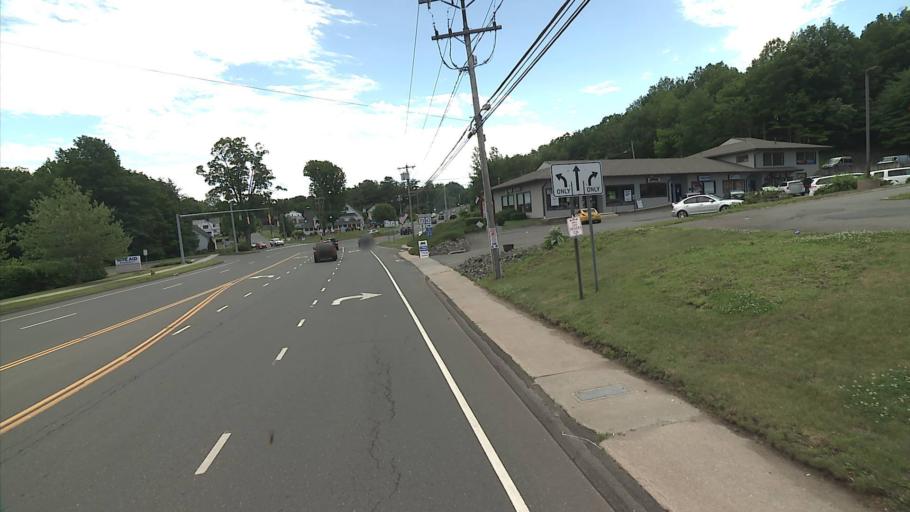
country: US
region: Connecticut
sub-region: Litchfield County
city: Watertown
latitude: 41.5913
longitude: -73.1069
